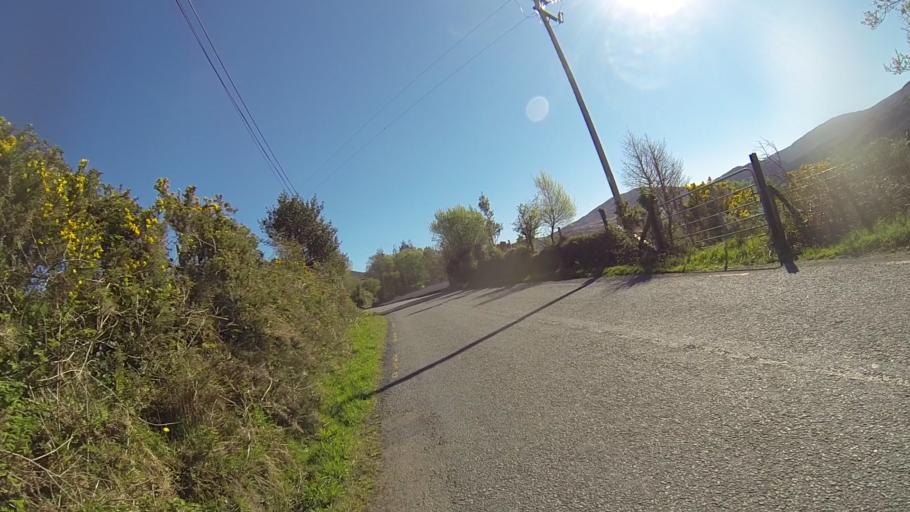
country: IE
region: Munster
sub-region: Ciarrai
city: Kenmare
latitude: 51.7689
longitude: -9.7579
